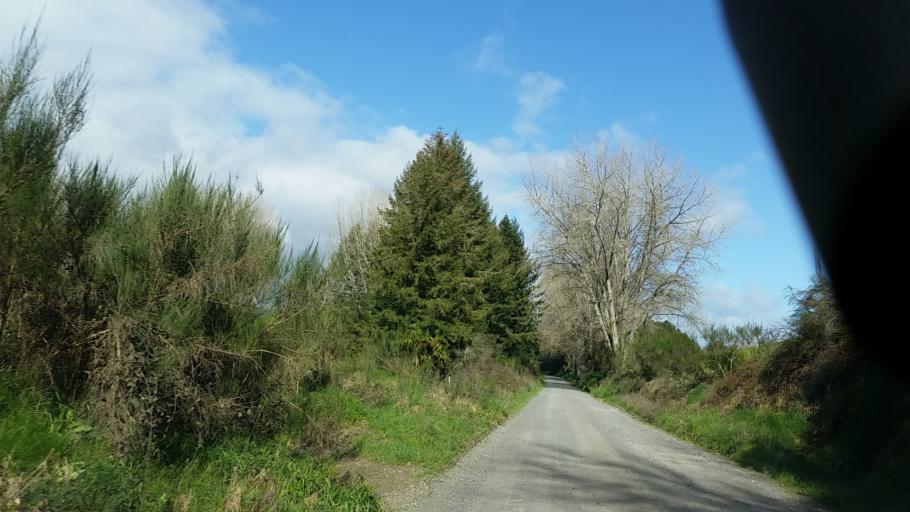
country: NZ
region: Waikato
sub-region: South Waikato District
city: Tokoroa
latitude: -38.3807
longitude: 176.0843
